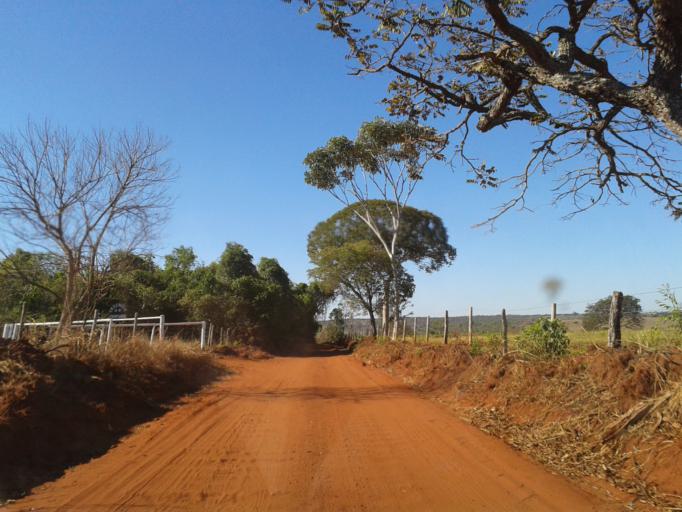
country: BR
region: Minas Gerais
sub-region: Ituiutaba
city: Ituiutaba
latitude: -19.0705
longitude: -49.3295
